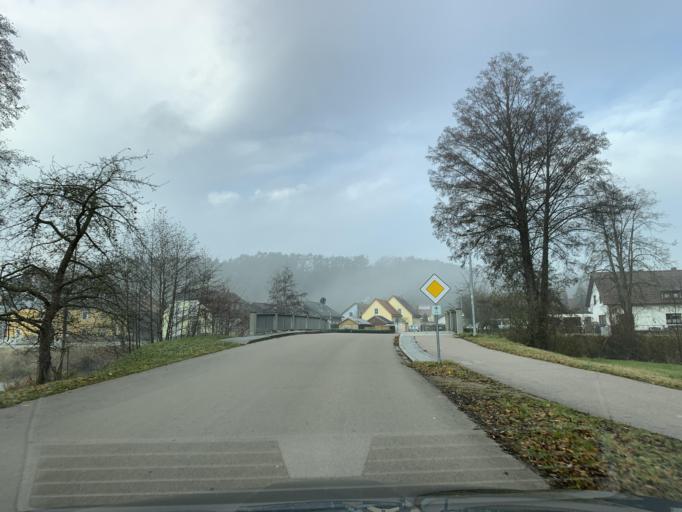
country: DE
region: Bavaria
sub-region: Upper Palatinate
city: Neunburg vorm Wald
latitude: 49.3631
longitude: 12.3981
